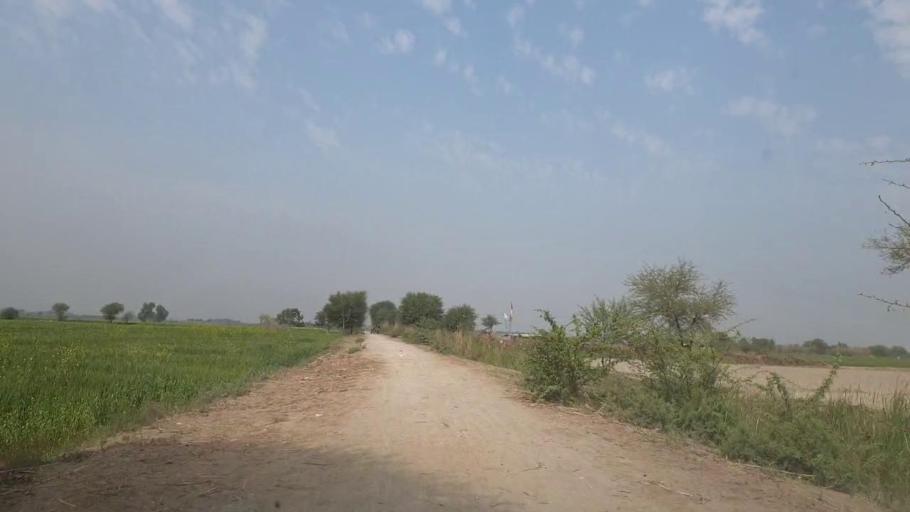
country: PK
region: Sindh
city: Mirpur Khas
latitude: 25.5591
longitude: 69.1076
